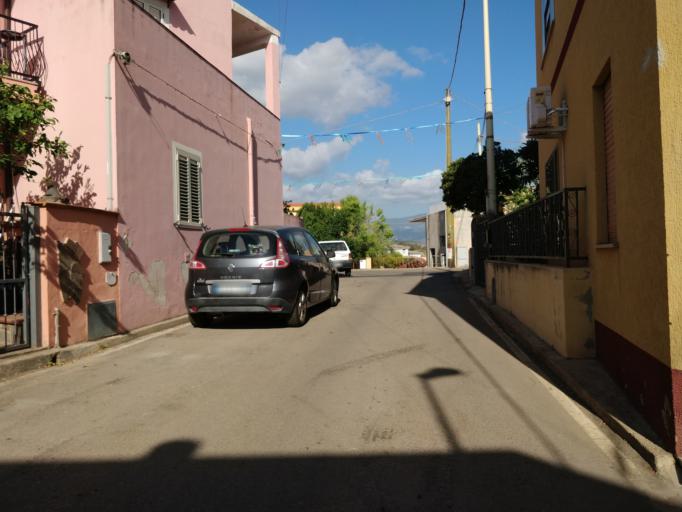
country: IT
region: Sardinia
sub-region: Provincia di Ogliastra
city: Girasole
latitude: 39.9531
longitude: 9.6620
